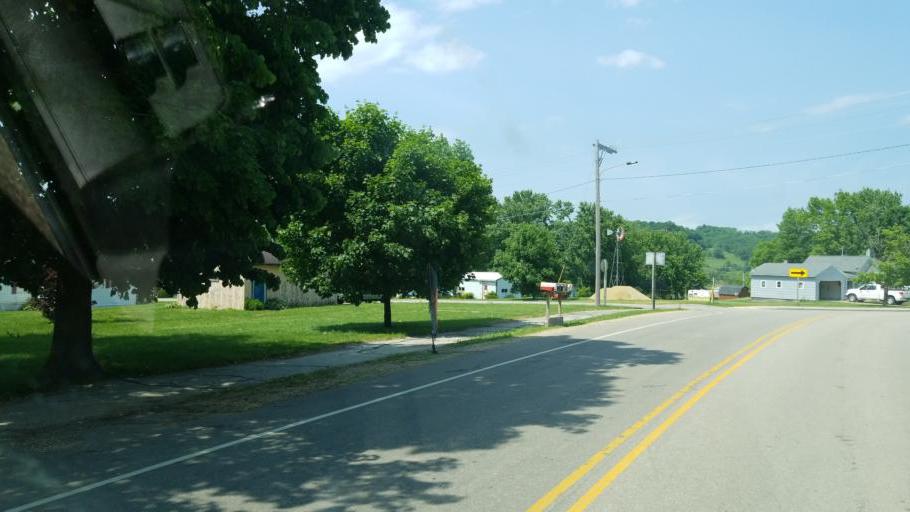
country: US
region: Wisconsin
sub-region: Vernon County
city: Viroqua
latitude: 43.5031
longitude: -90.6790
